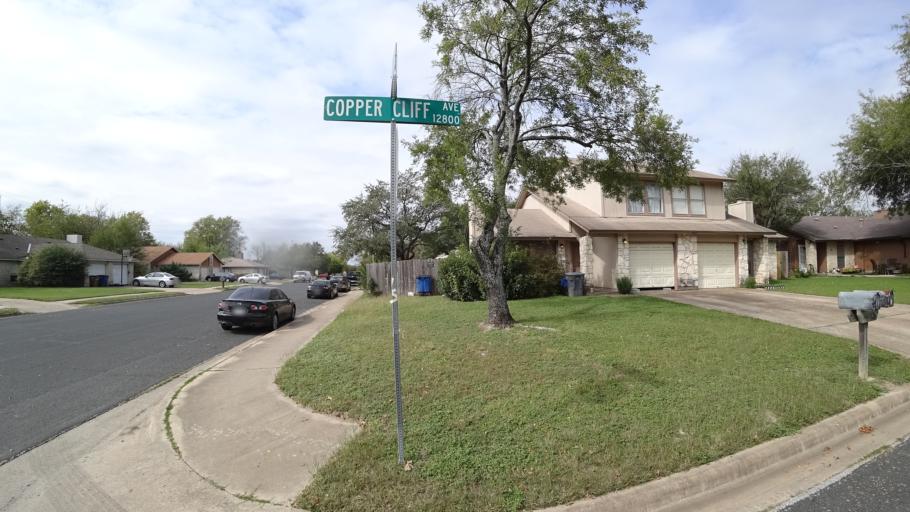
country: US
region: Texas
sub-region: Travis County
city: Wells Branch
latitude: 30.4220
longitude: -97.6965
